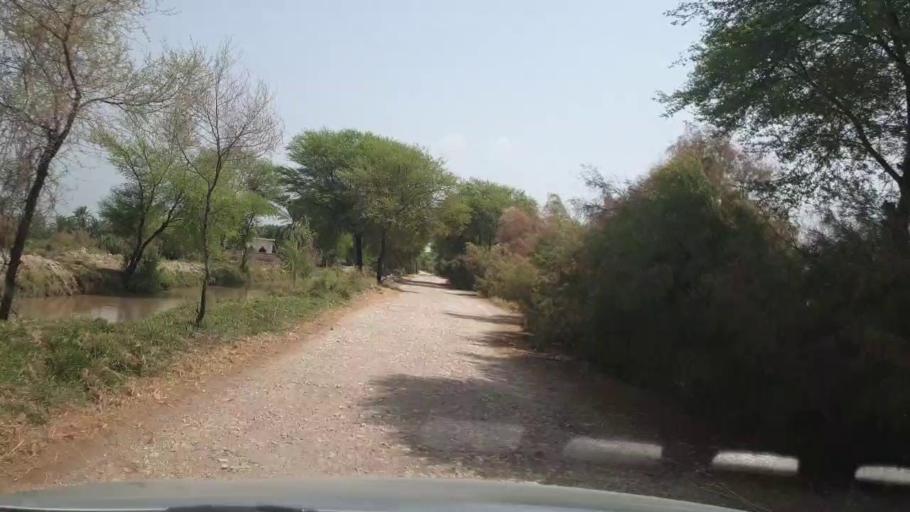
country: PK
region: Sindh
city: Garhi Yasin
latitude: 27.9328
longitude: 68.3644
